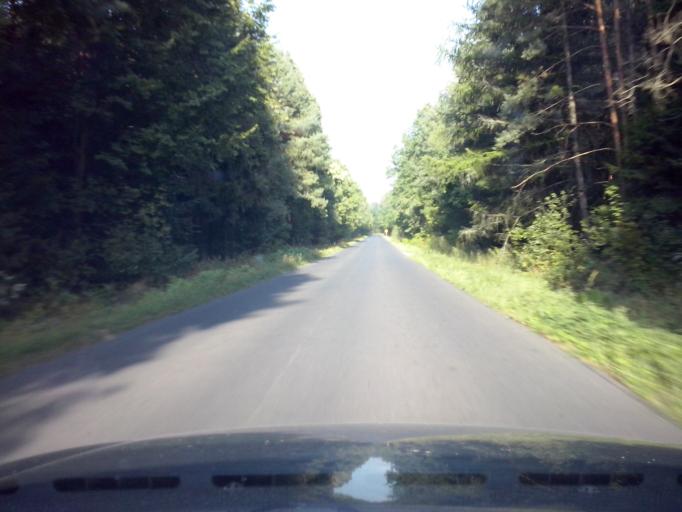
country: PL
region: Subcarpathian Voivodeship
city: Nowa Sarzyna
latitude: 50.3097
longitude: 22.3077
